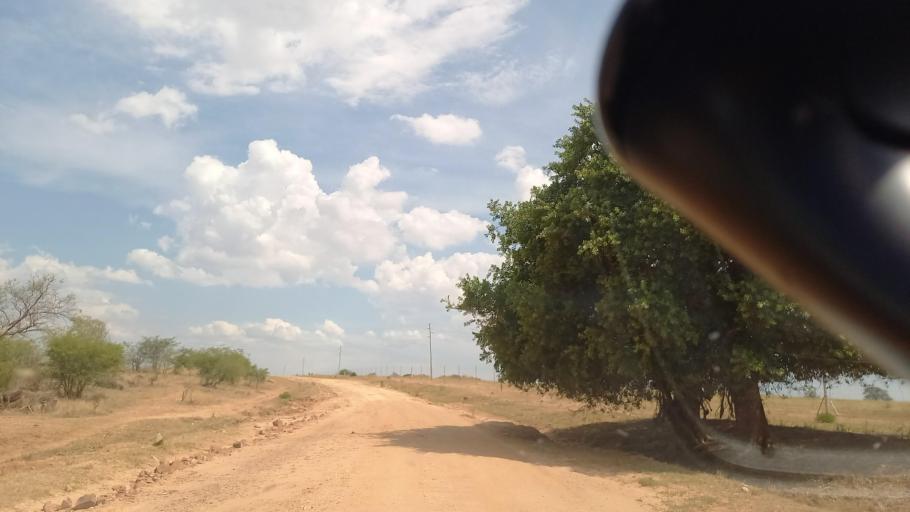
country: ZM
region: Southern
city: Nakambala
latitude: -16.1054
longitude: 28.0217
